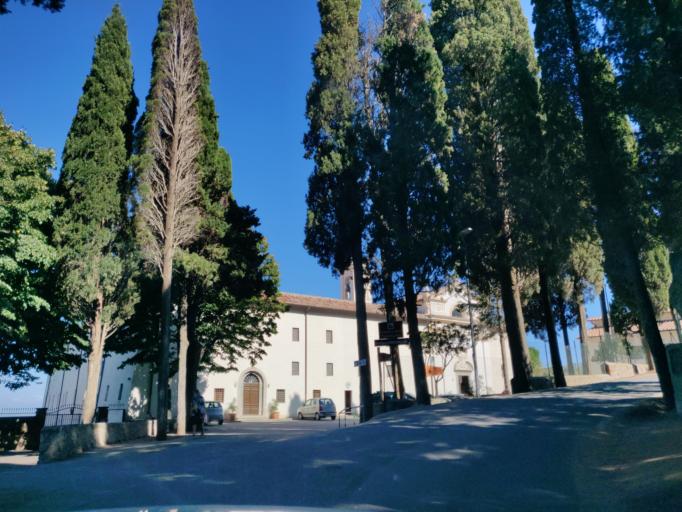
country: IT
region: Tuscany
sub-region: Provincia di Grosseto
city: Monte Argentario
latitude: 42.4139
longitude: 11.1602
